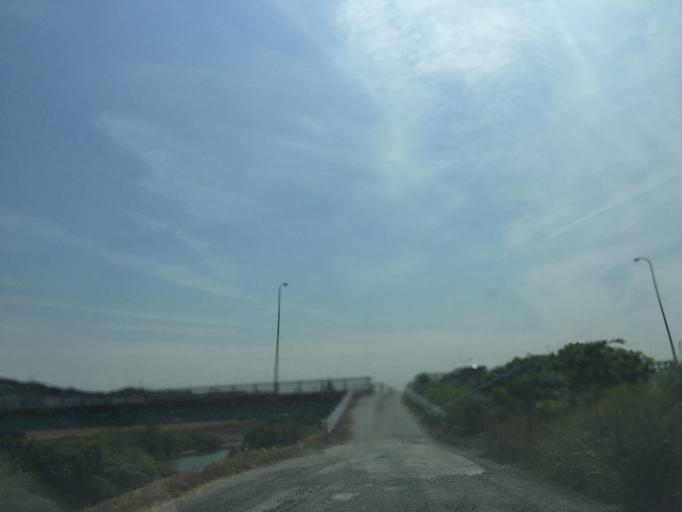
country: JP
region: Shizuoka
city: Fukuroi
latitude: 34.7527
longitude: 137.9543
